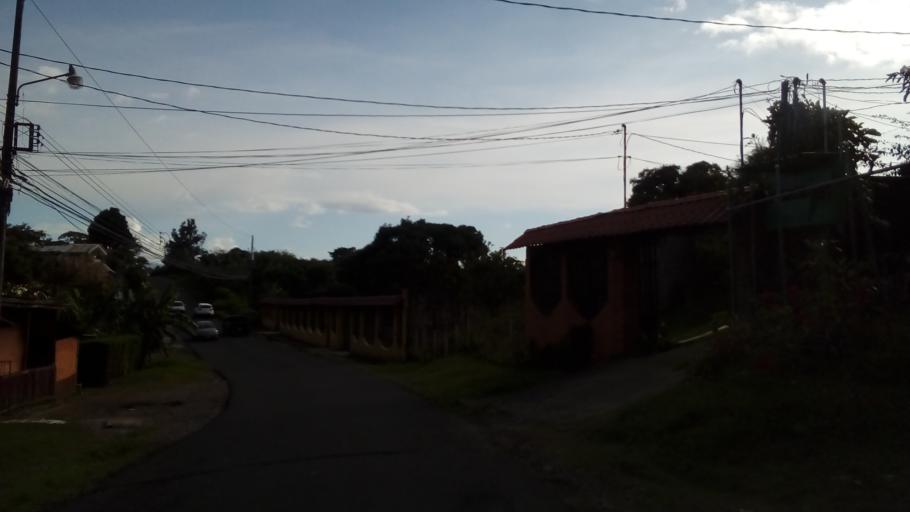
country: CR
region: Heredia
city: Angeles
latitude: 9.9988
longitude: -84.0524
